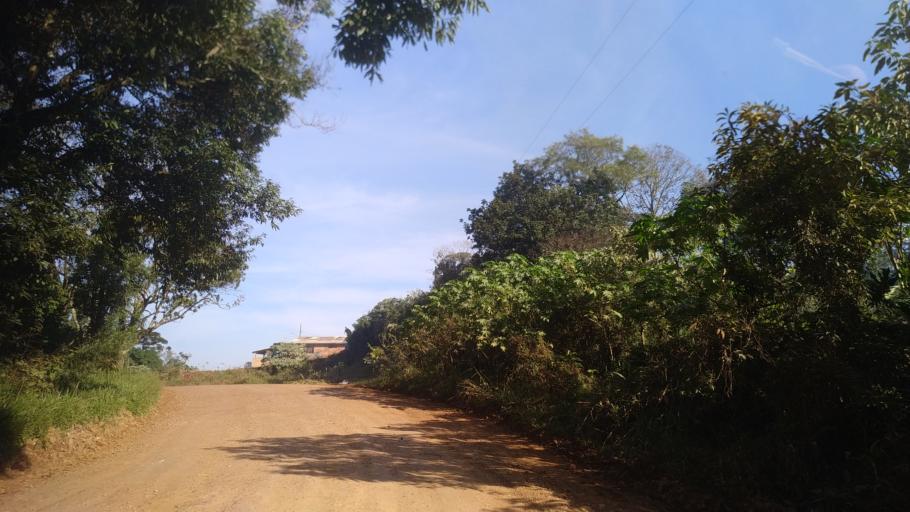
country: BR
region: Santa Catarina
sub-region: Chapeco
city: Chapeco
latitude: -27.1248
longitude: -52.6259
